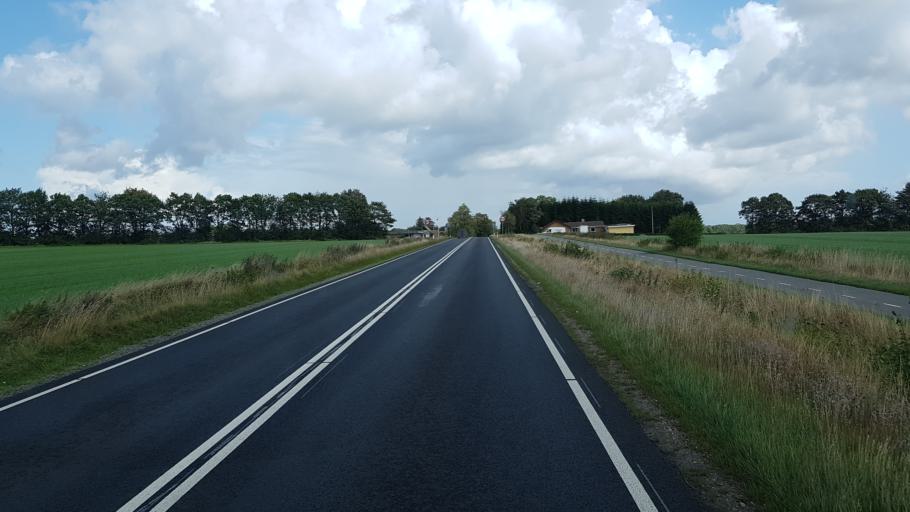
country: DK
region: South Denmark
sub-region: Vejen Kommune
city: Vejen
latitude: 55.5599
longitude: 9.1256
